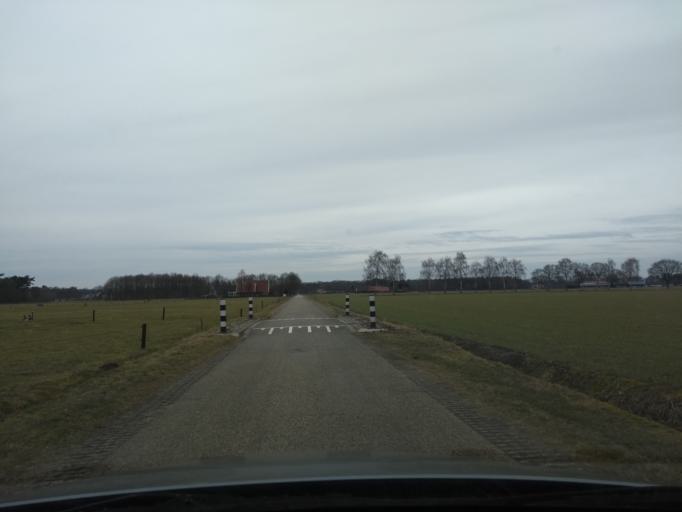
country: NL
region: Overijssel
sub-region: Gemeente Borne
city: Borne
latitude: 52.3546
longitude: 6.7324
